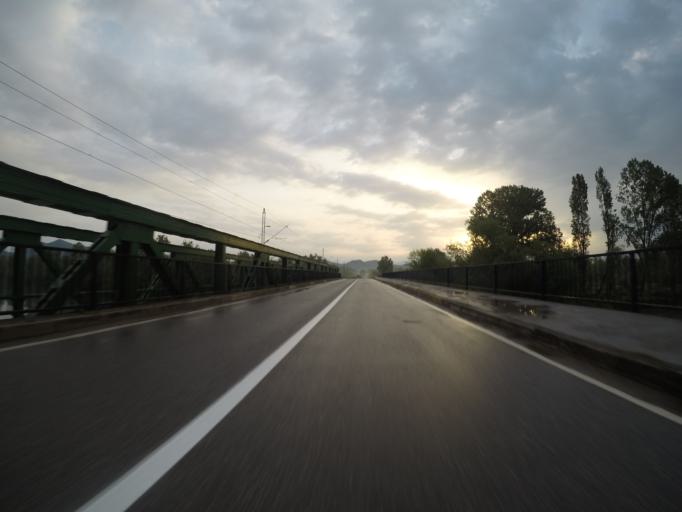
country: ME
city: Mojanovici
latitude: 42.2918
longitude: 19.1533
